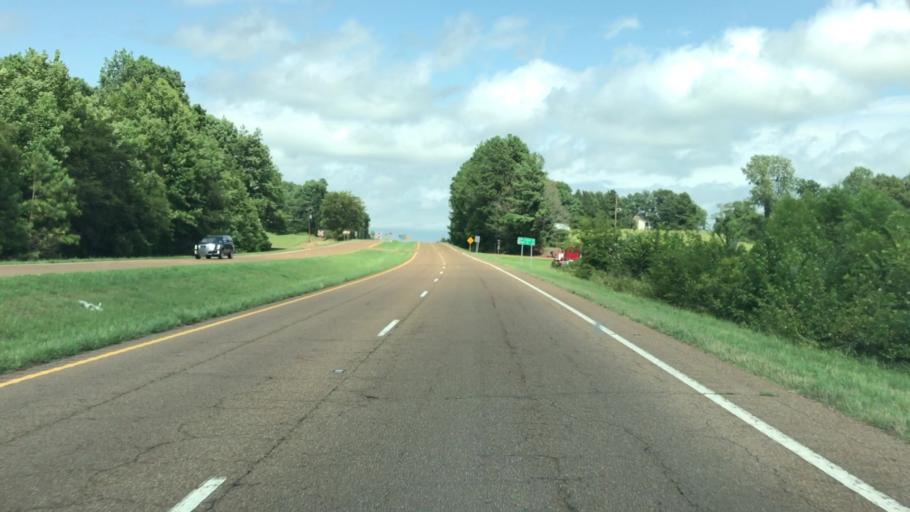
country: US
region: Tennessee
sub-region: Obion County
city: Englewood
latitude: 36.3546
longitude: -89.1393
